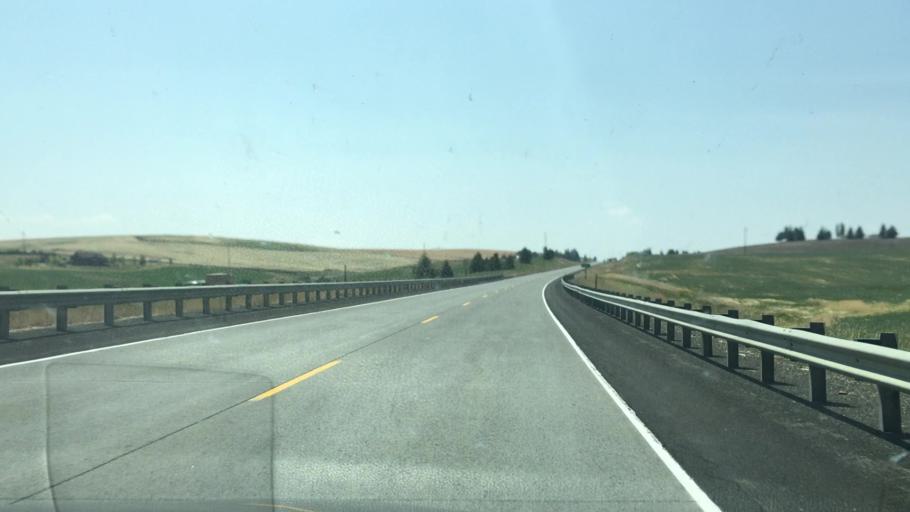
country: US
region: Idaho
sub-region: Lewis County
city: Nezperce
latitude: 46.0691
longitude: -116.3416
